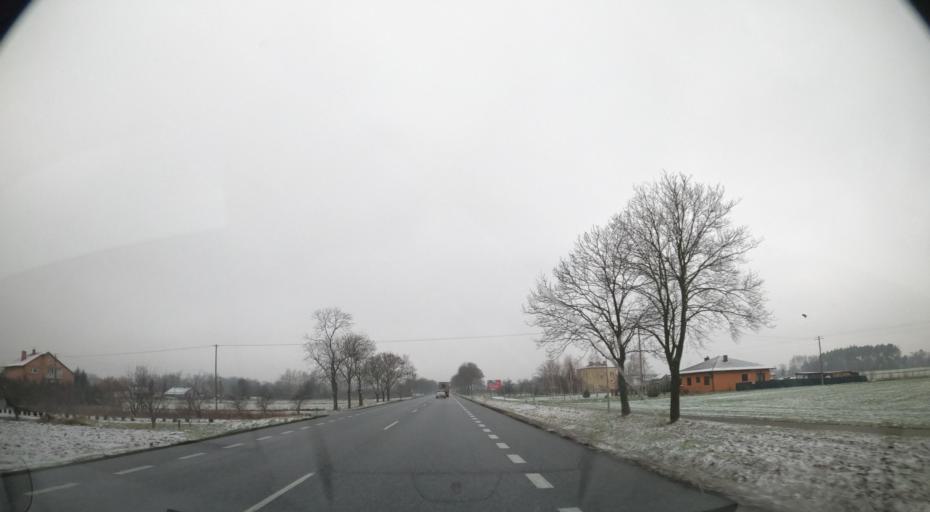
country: PL
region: Masovian Voivodeship
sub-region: Powiat sochaczewski
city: Sochaczew
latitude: 52.2221
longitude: 20.3196
